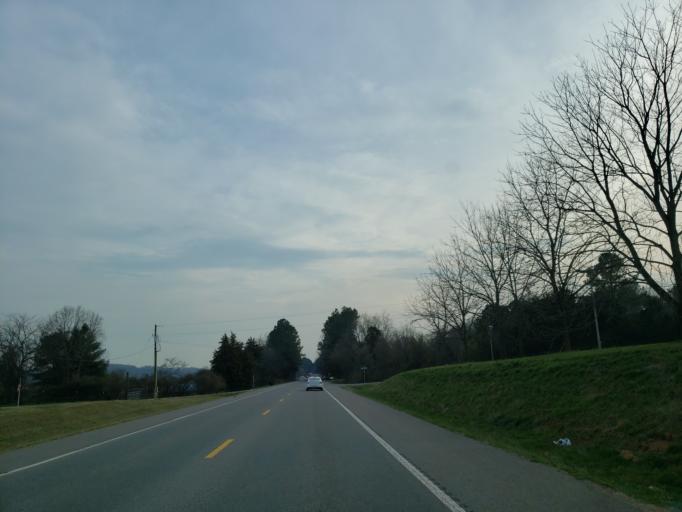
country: US
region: Tennessee
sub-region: Bradley County
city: Wildwood Lake
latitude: 35.0427
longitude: -84.9041
